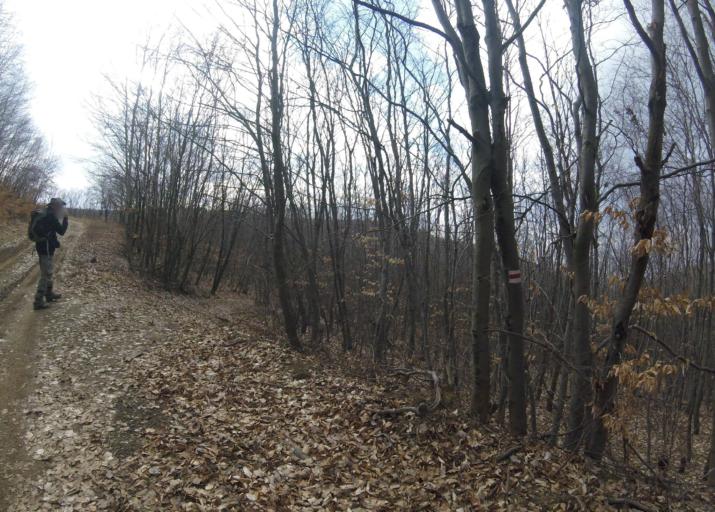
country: HU
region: Heves
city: Belapatfalva
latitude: 48.0319
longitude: 20.3581
